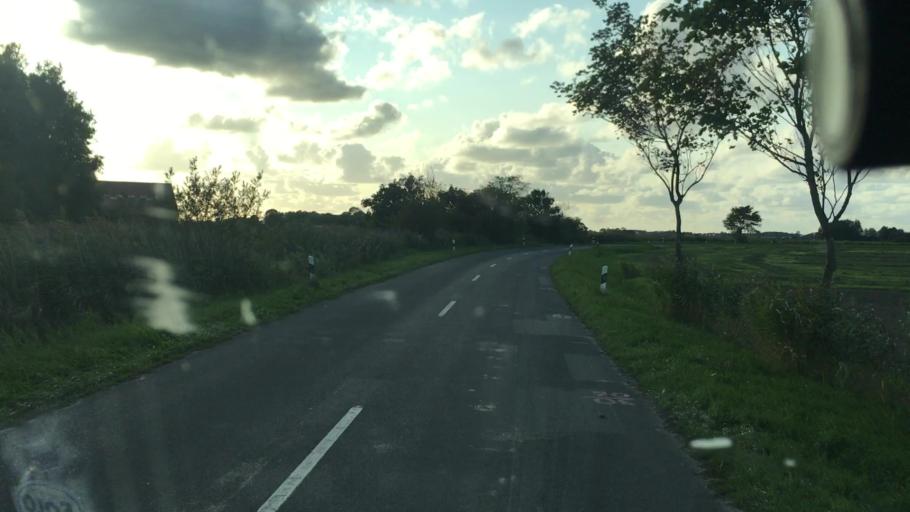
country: DE
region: Lower Saxony
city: Werdum
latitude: 53.6687
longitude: 7.7267
